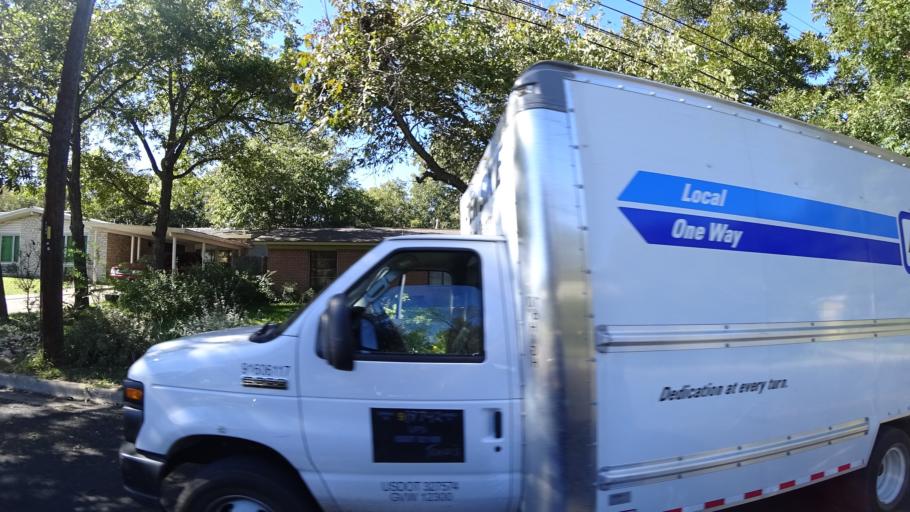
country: US
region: Texas
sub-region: Travis County
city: Rollingwood
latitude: 30.2458
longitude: -97.7756
